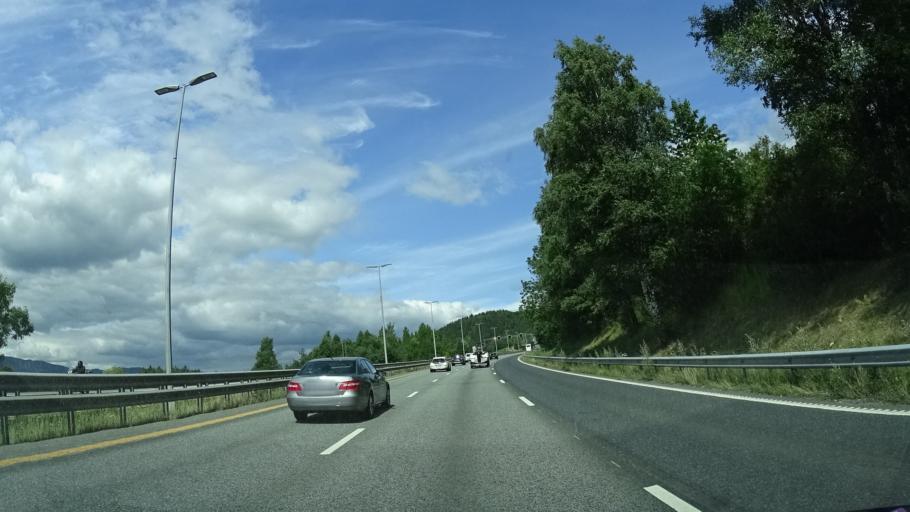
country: NO
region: Buskerud
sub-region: Lier
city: Tranby
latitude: 59.7833
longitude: 10.2738
